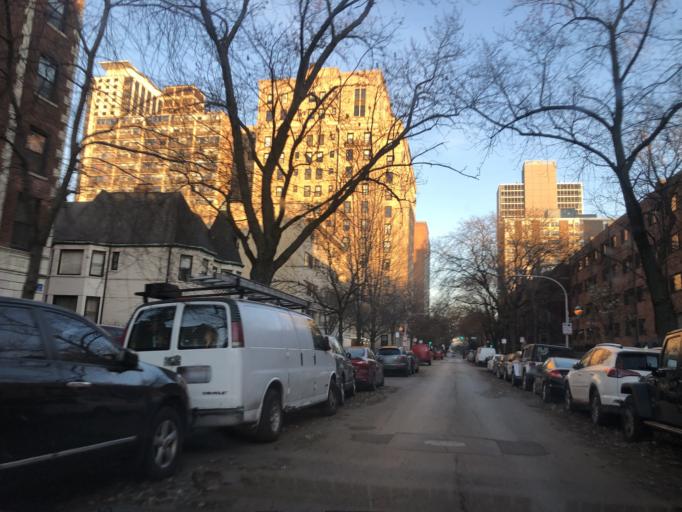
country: US
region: Illinois
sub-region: Cook County
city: Chicago
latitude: 41.9377
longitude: -87.6414
